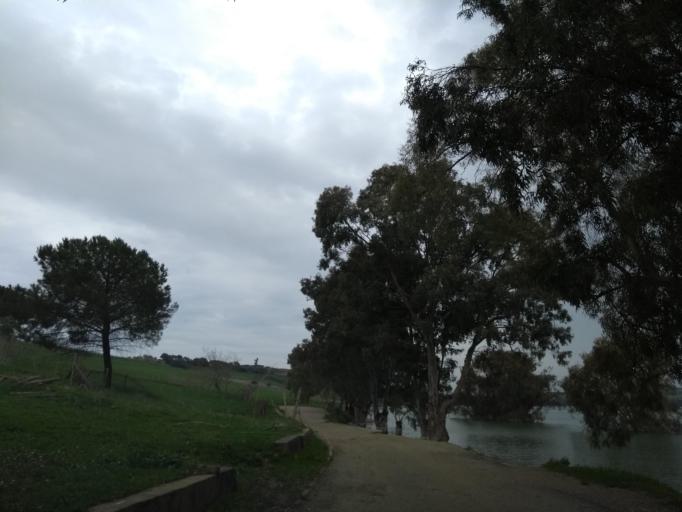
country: IT
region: Sicily
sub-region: Palermo
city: Partinico
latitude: 37.9909
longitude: 13.0826
